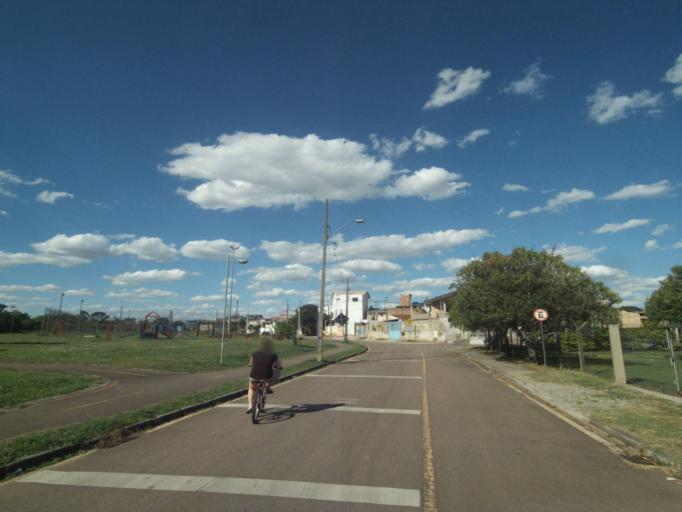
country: BR
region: Parana
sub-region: Curitiba
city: Curitiba
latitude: -25.5110
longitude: -49.3379
